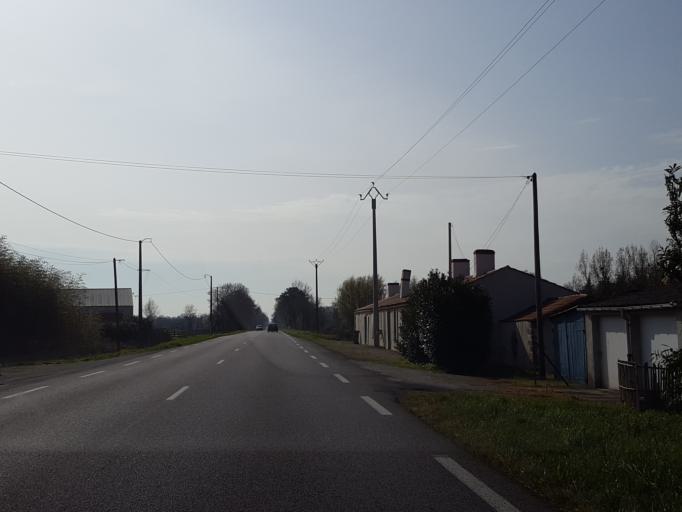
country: FR
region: Pays de la Loire
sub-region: Departement de la Vendee
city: Les Lucs-sur-Boulogne
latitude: 46.8324
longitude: -1.4828
